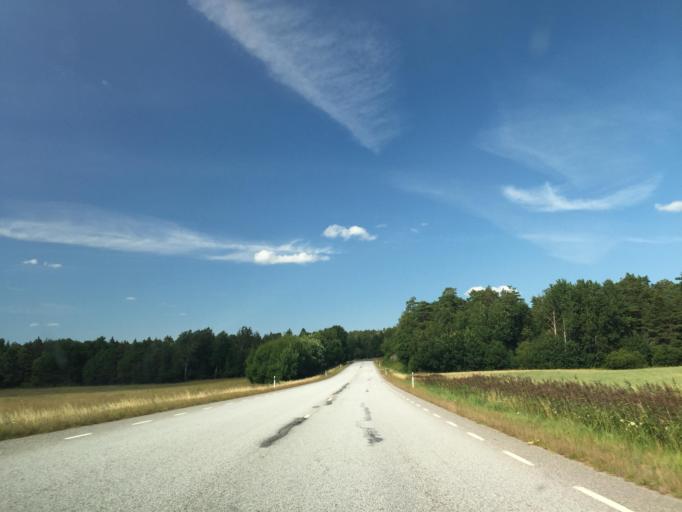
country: SE
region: Vaestra Goetaland
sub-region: Tanums Kommun
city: Tanumshede
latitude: 58.8143
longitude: 11.2627
